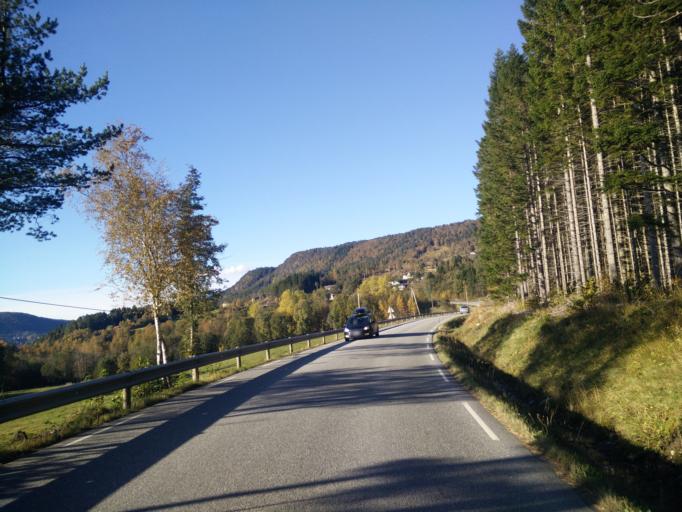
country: NO
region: More og Romsdal
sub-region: Halsa
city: Liaboen
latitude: 63.1137
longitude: 8.3227
